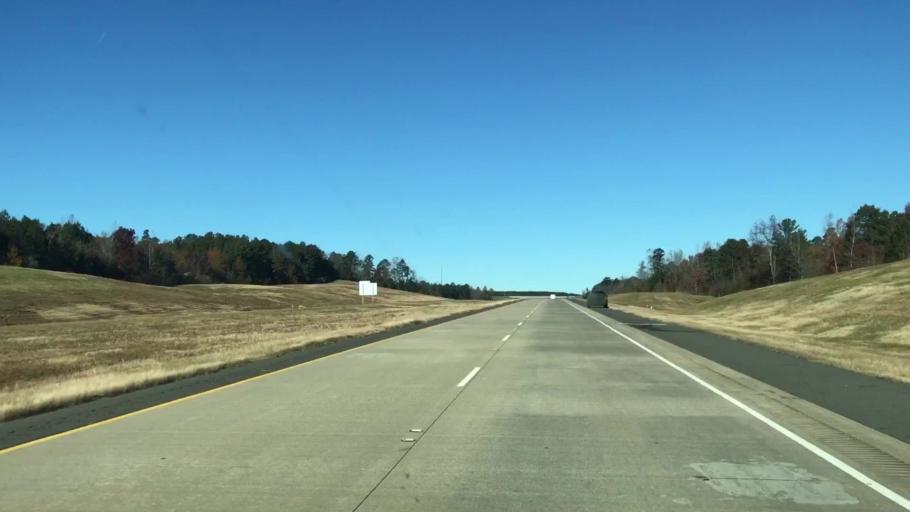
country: US
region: Louisiana
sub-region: Caddo Parish
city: Vivian
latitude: 32.9128
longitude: -93.8735
